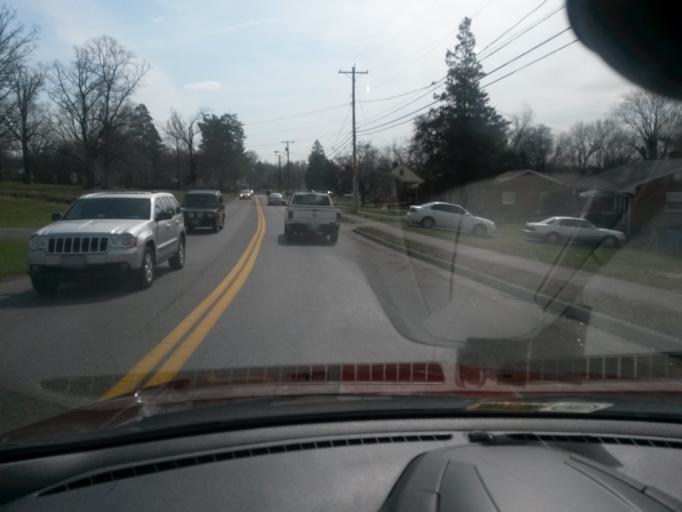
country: US
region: Virginia
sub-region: City of Roanoke
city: Roanoke
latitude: 37.3020
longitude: -79.9799
